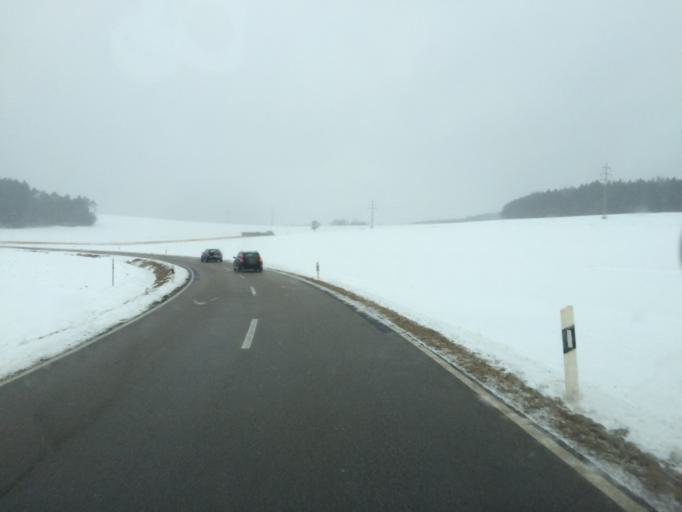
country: DE
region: Bavaria
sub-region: Upper Palatinate
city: Ensdorf
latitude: 49.3478
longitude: 11.9625
